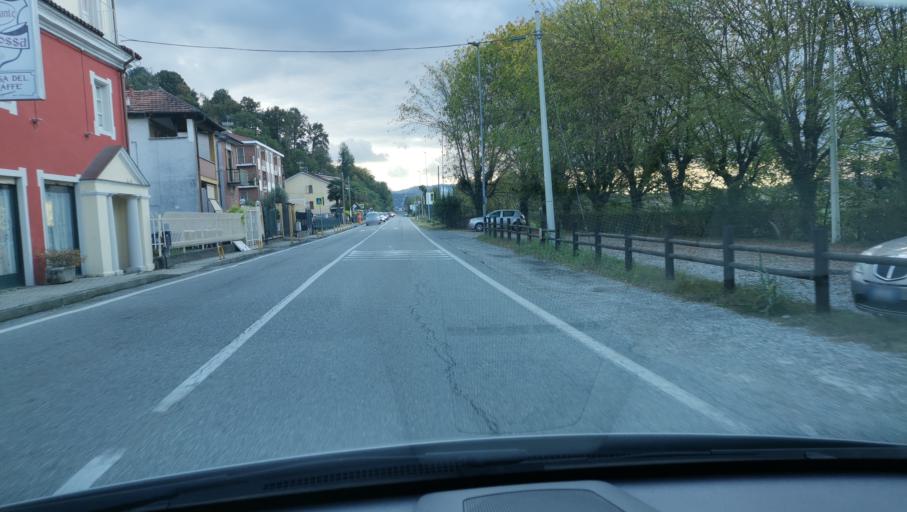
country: IT
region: Piedmont
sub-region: Provincia di Torino
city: Piana San Raffaele
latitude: 45.1656
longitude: 7.8577
